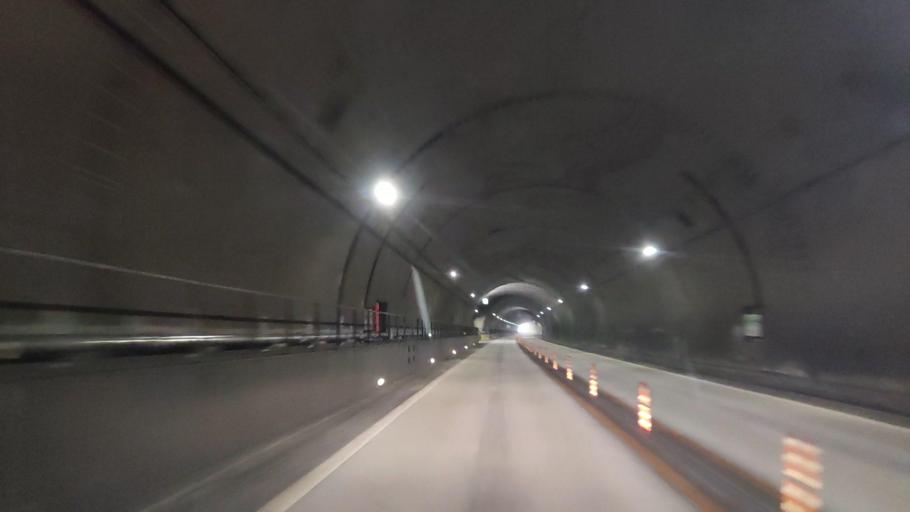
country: JP
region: Ehime
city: Hojo
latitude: 34.0823
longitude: 132.9771
